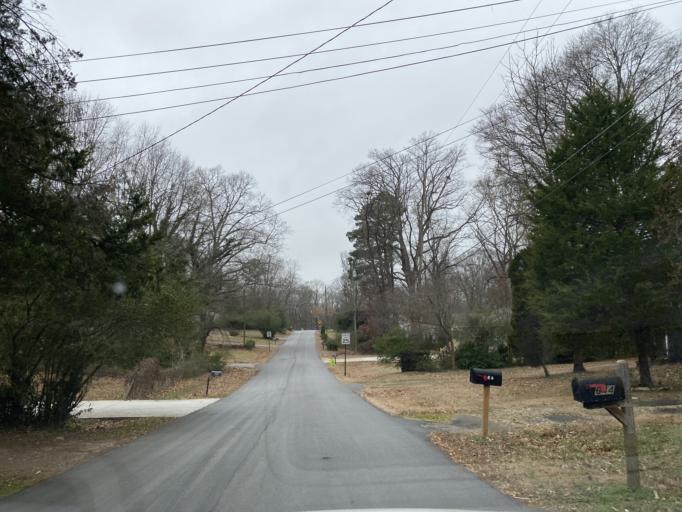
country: US
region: Georgia
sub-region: Cobb County
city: Fair Oaks
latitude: 33.9018
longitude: -84.5720
